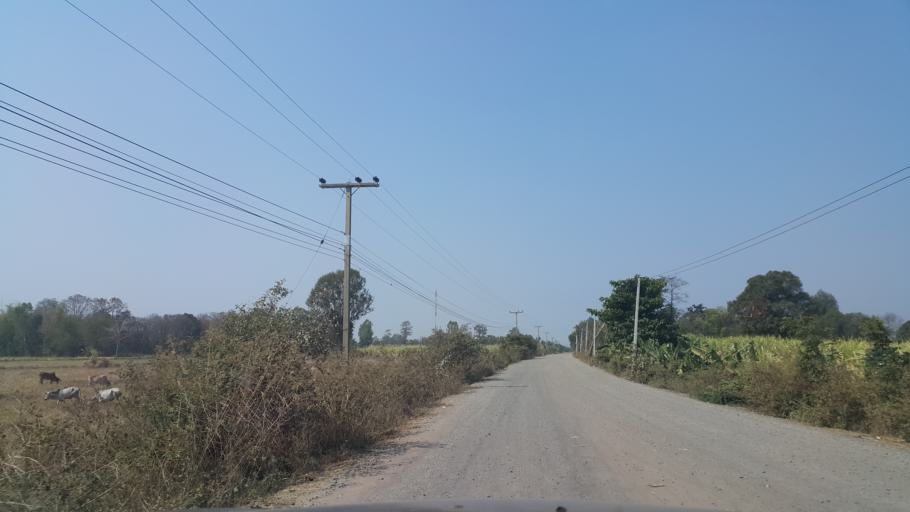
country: TH
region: Buriram
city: Satuek
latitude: 15.1328
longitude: 103.3546
